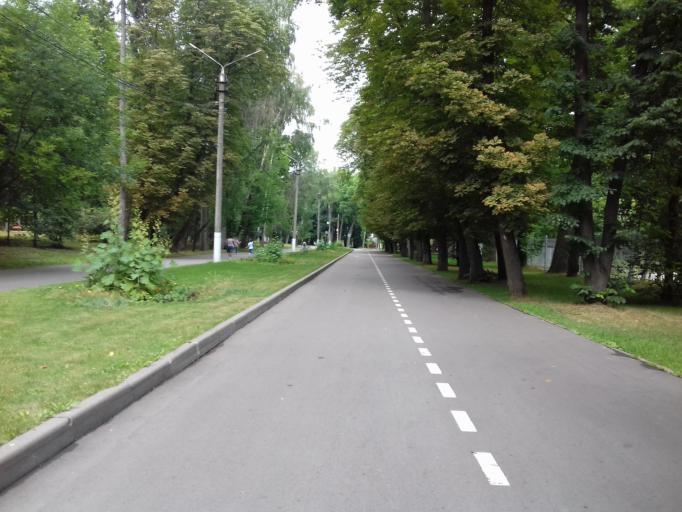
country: RU
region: Tula
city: Tula
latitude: 54.1822
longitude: 37.5967
